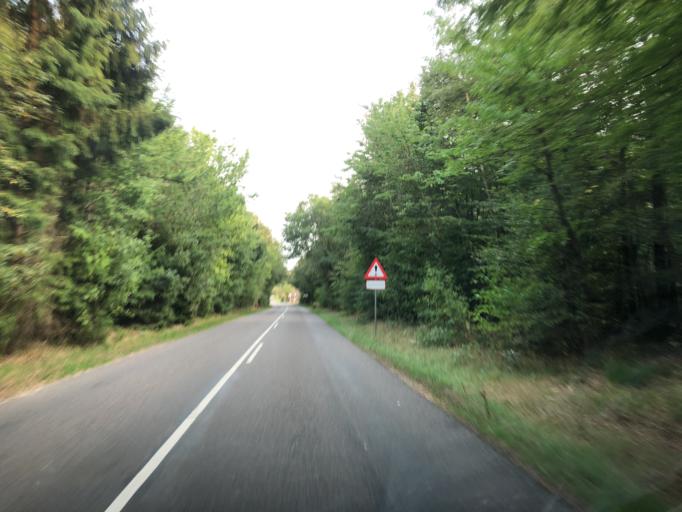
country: DK
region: Central Jutland
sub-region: Ringkobing-Skjern Kommune
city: Videbaek
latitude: 56.0589
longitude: 8.6864
